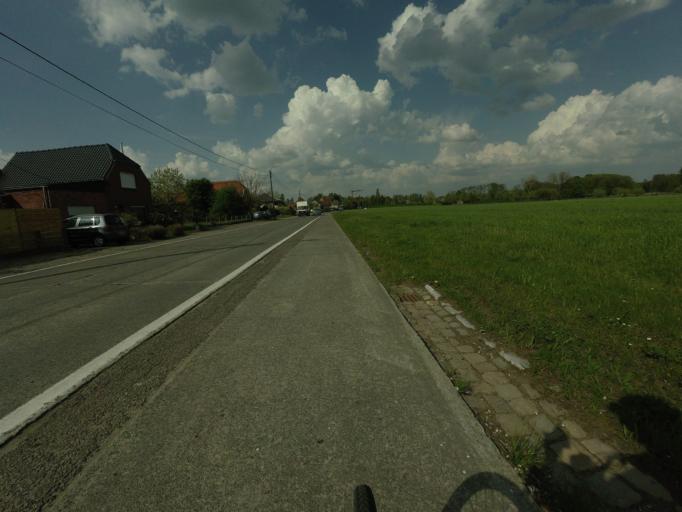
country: BE
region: Flanders
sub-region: Provincie Antwerpen
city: Putte
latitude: 51.0670
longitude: 4.6561
